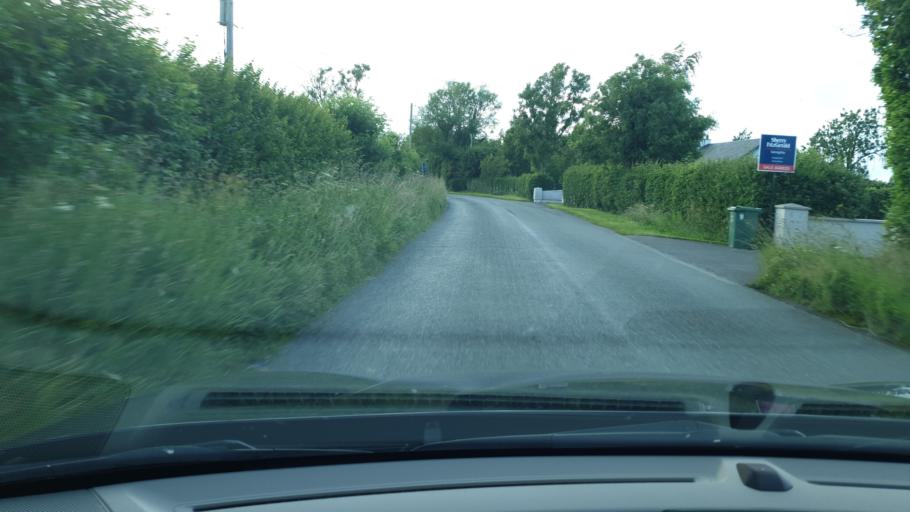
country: IE
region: Leinster
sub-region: An Mhi
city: Ashbourne
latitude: 53.5331
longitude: -6.4287
